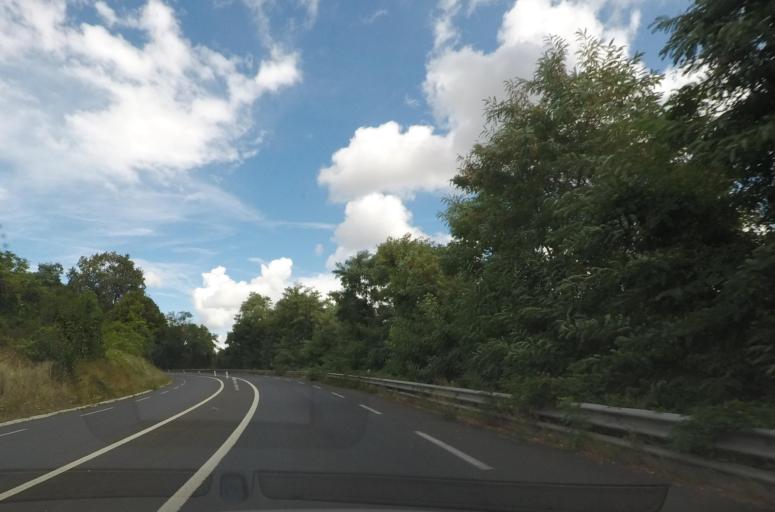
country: FR
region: Pays de la Loire
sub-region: Departement de la Sarthe
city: Clermont-Creans
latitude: 47.7246
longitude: -0.0093
